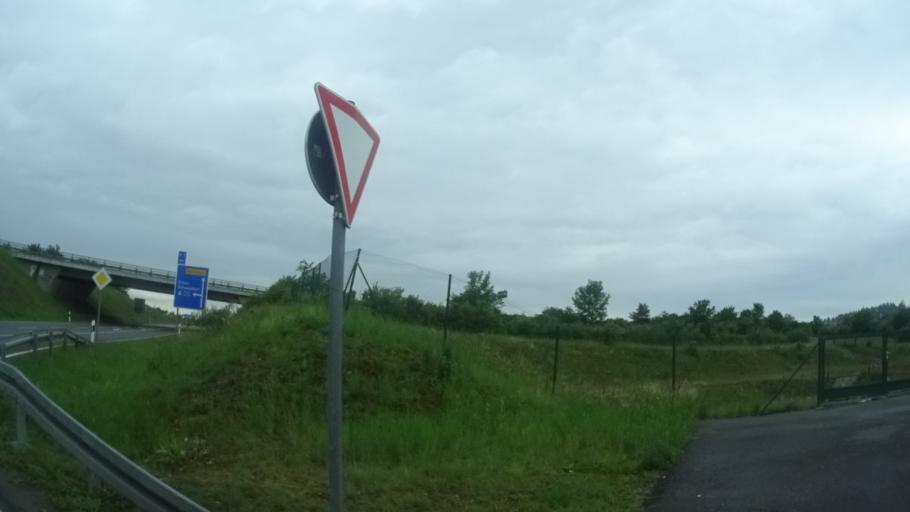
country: DE
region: Thuringia
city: Rohr
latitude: 50.5810
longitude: 10.4771
